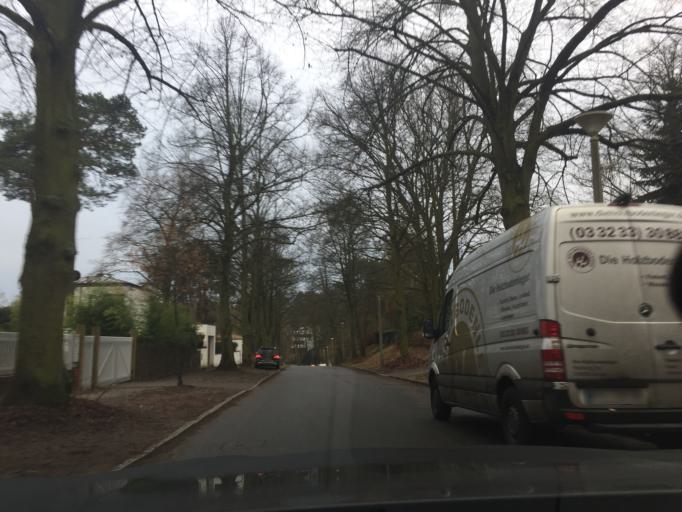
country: DE
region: Berlin
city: Kladow
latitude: 52.4601
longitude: 13.1059
